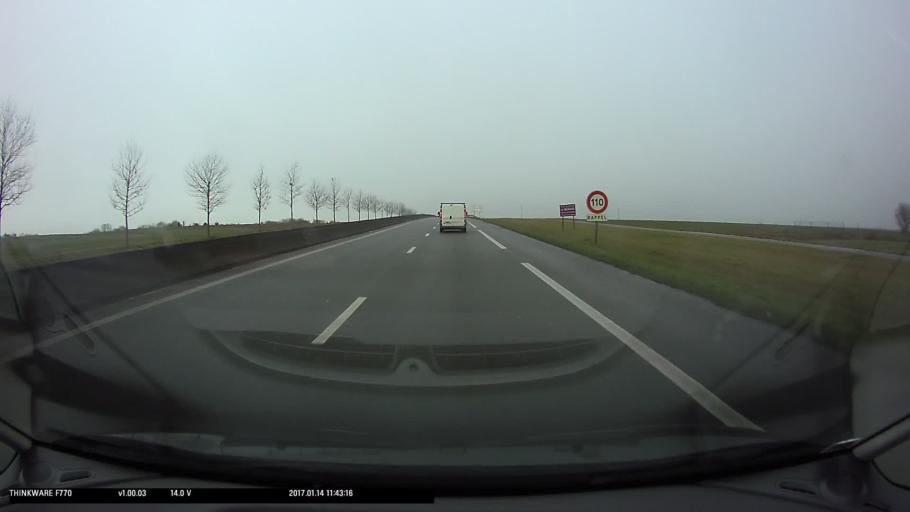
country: FR
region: Ile-de-France
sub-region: Departement du Val-d'Oise
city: Vigny
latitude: 49.0767
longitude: 1.9463
